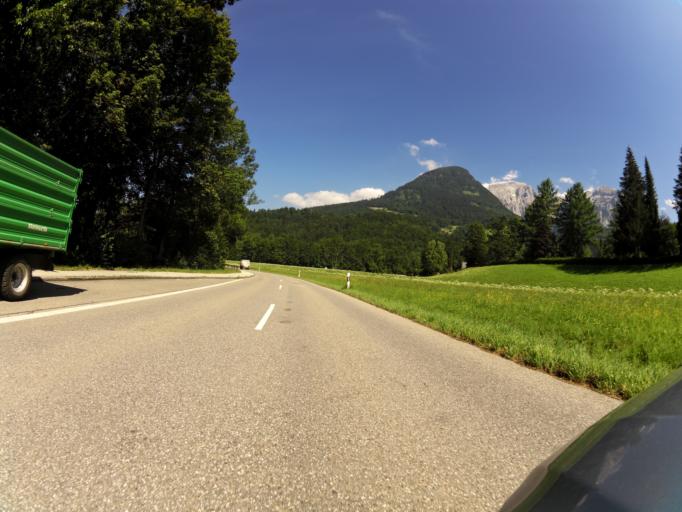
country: DE
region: Bavaria
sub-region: Upper Bavaria
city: Berchtesgaden
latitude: 47.6225
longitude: 12.9940
